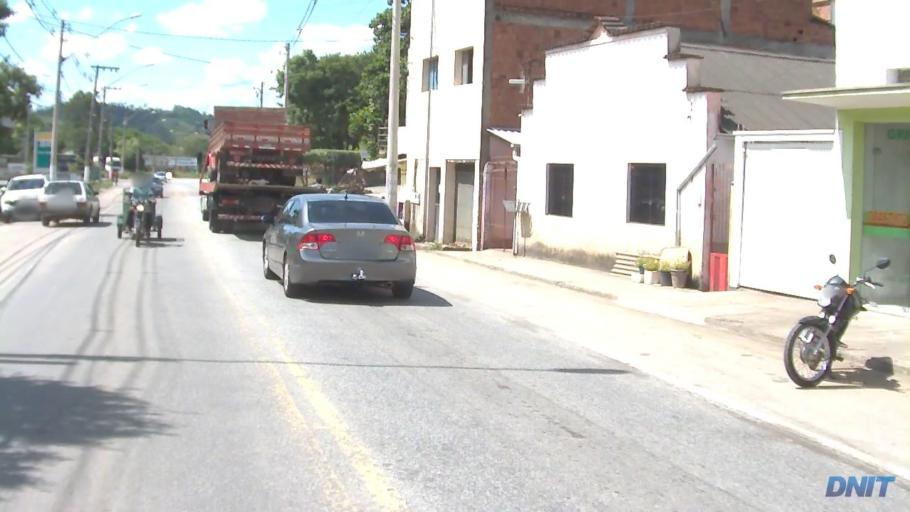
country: BR
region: Minas Gerais
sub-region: Coronel Fabriciano
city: Coronel Fabriciano
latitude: -19.5306
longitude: -42.6650
